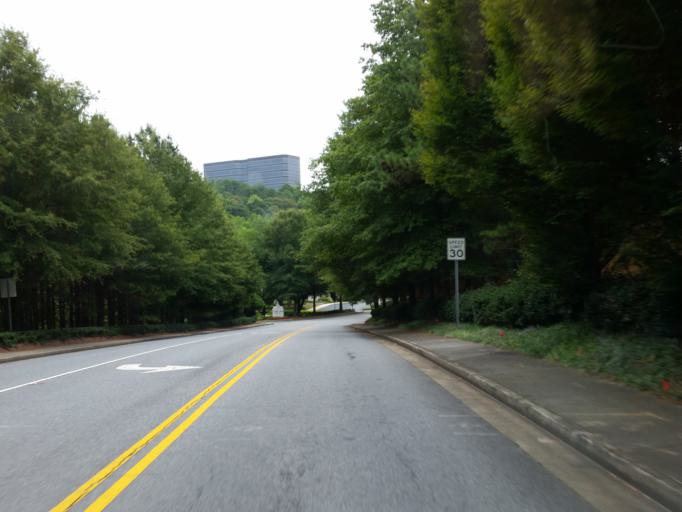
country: US
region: Georgia
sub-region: Cobb County
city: Vinings
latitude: 33.8961
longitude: -84.4606
